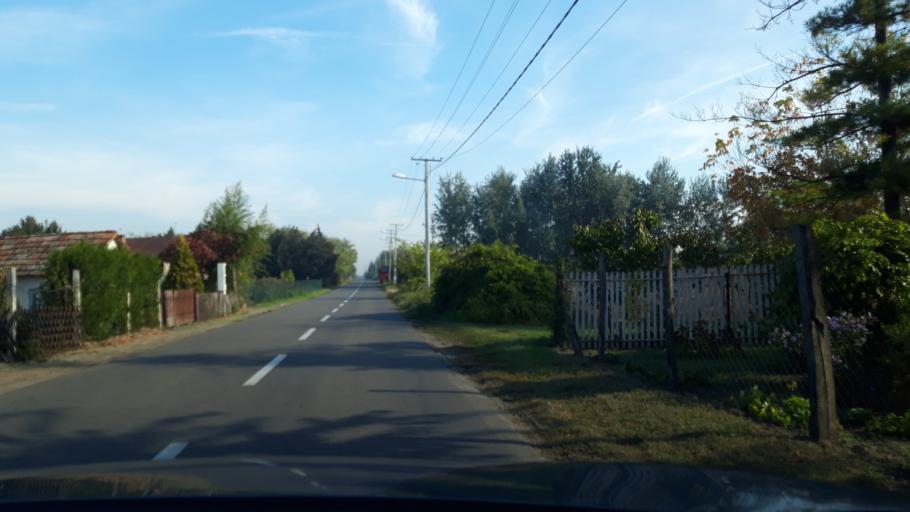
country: HU
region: Csongrad
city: Asotthalom
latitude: 46.1154
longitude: 19.8415
